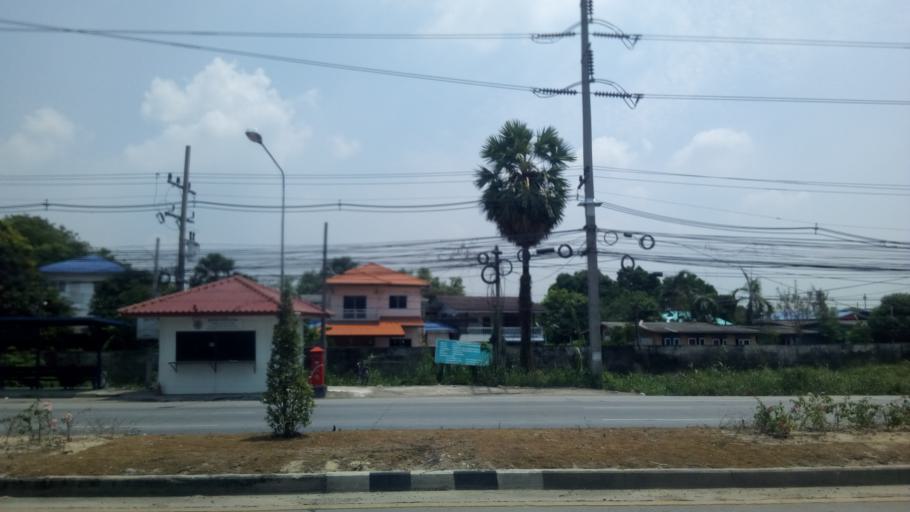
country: TH
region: Pathum Thani
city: Pathum Thani
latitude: 14.0220
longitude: 100.5426
